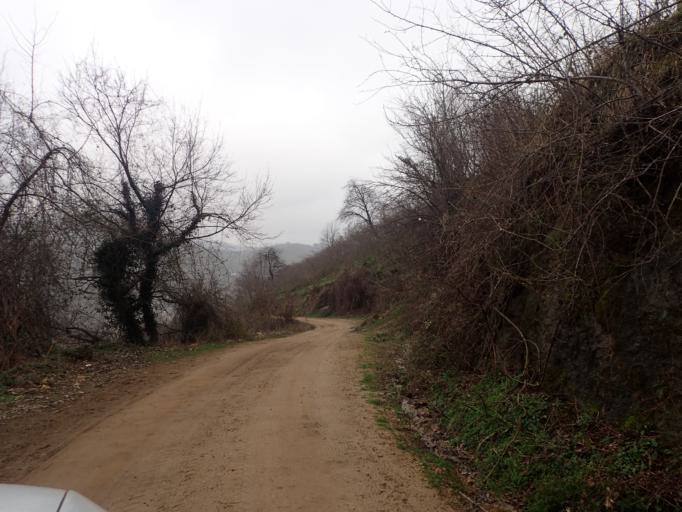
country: TR
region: Ordu
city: Camas
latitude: 40.9109
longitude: 37.5612
